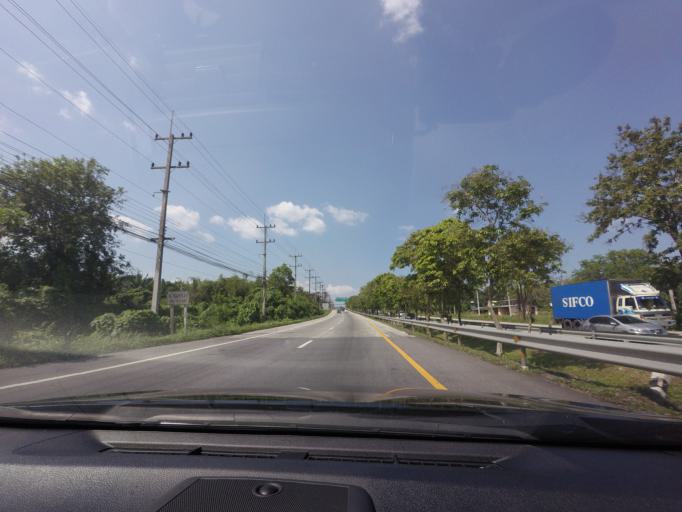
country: TH
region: Prachuap Khiri Khan
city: Bang Saphan Noi
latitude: 10.9281
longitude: 99.2898
